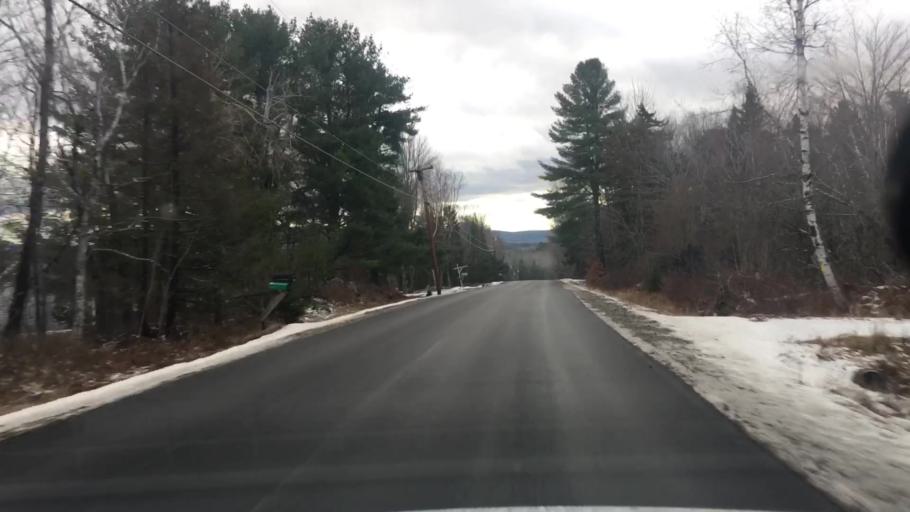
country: US
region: Maine
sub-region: Hancock County
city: Dedham
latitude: 44.6560
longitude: -68.7042
